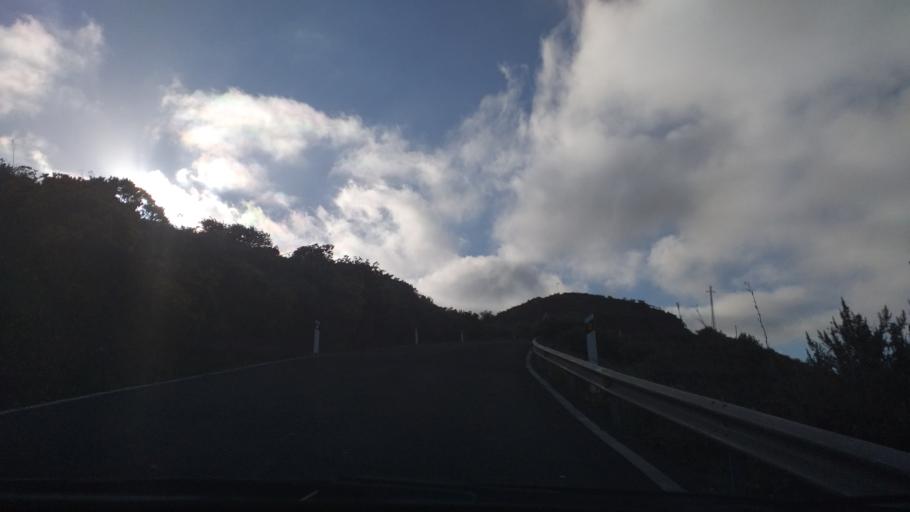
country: ES
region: Canary Islands
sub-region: Provincia de Las Palmas
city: Valsequillo de Gran Canaria
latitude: 27.9572
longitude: -15.4965
